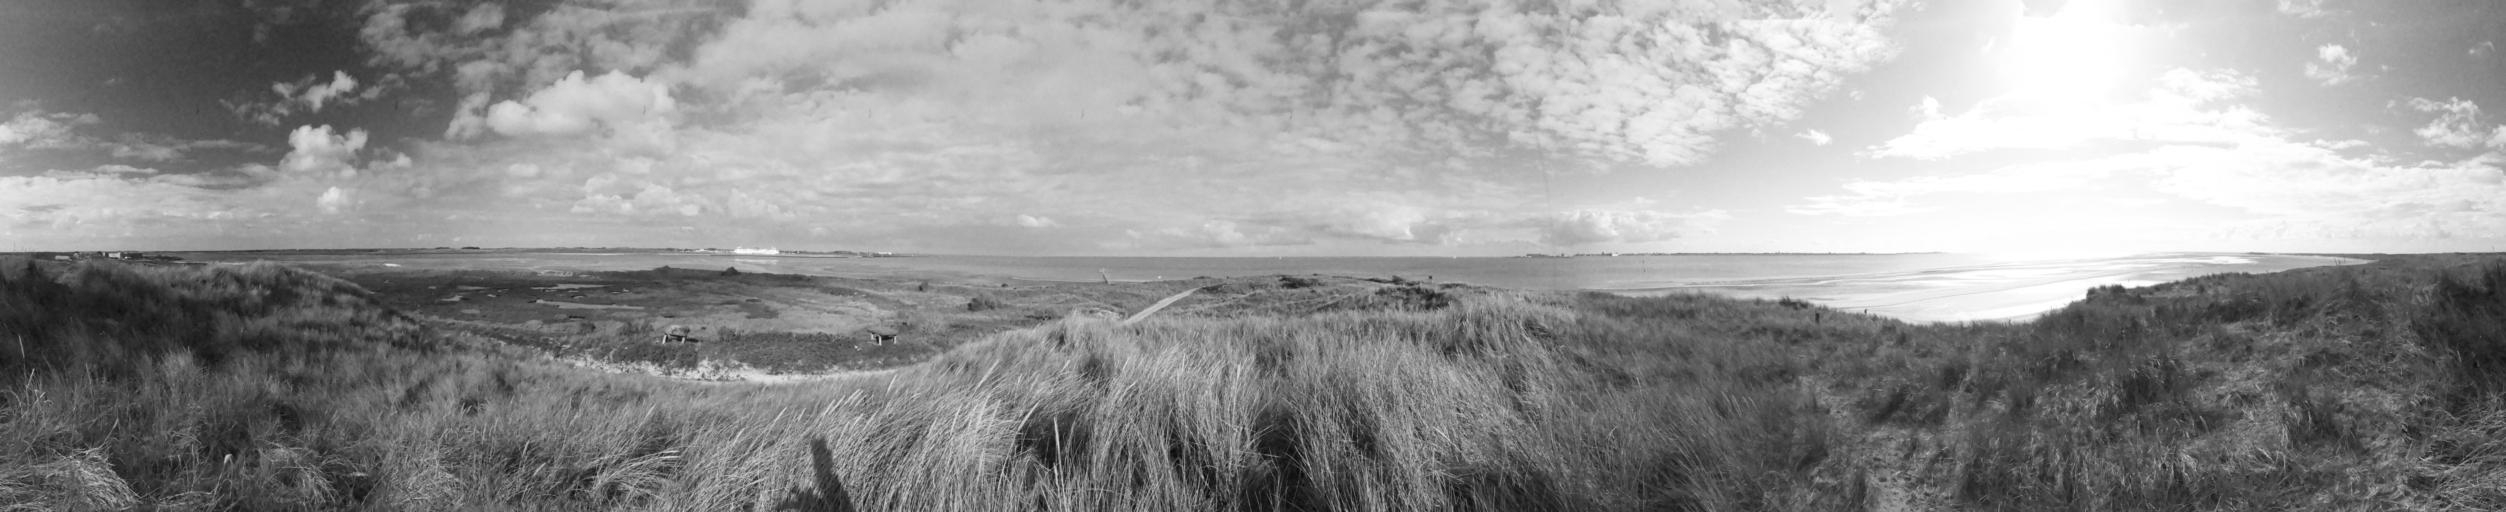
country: NL
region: North Holland
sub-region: Gemeente Den Helder
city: Den Helder
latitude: 52.9969
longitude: 4.7711
